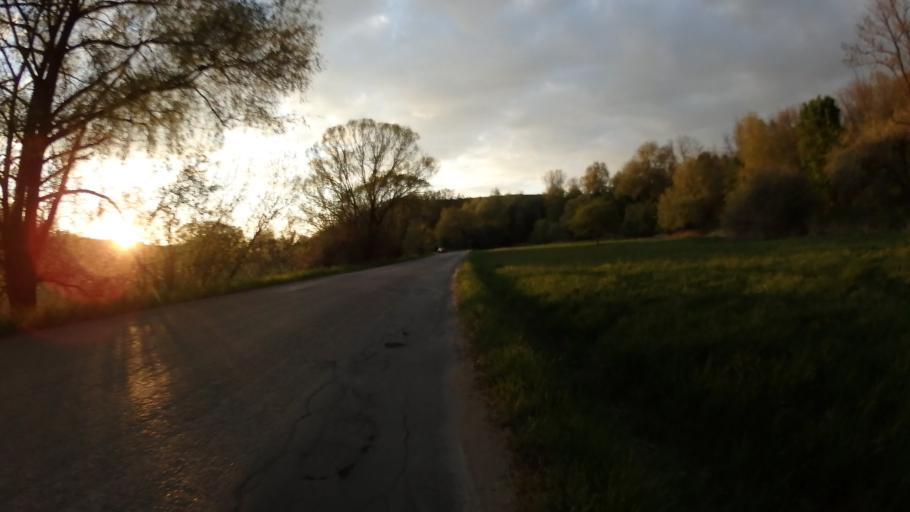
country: CZ
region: South Moravian
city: Strelice
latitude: 49.1488
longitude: 16.4651
